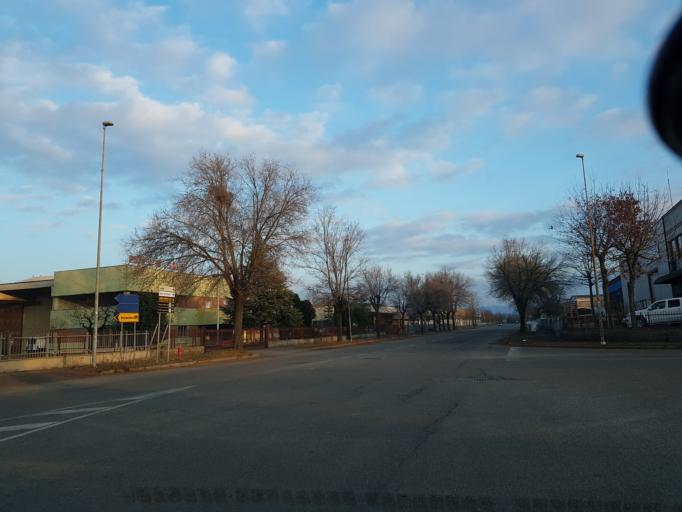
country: IT
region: Piedmont
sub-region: Provincia di Alessandria
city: Novi Ligure
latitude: 44.7563
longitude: 8.8084
